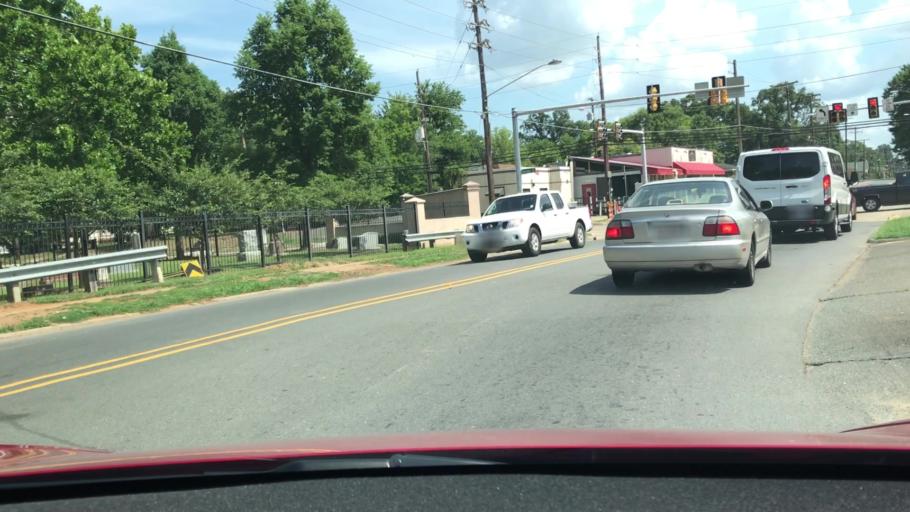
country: US
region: Louisiana
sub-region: Bossier Parish
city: Bossier City
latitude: 32.5004
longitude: -93.7333
